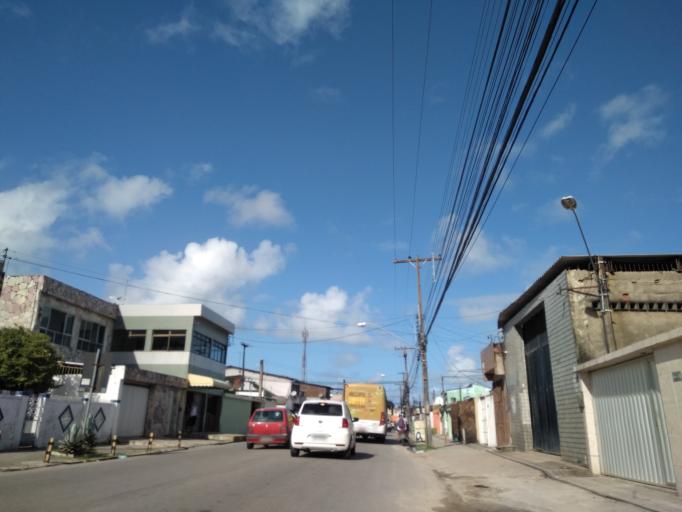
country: BR
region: Pernambuco
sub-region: Recife
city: Recife
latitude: -8.0769
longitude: -34.9104
